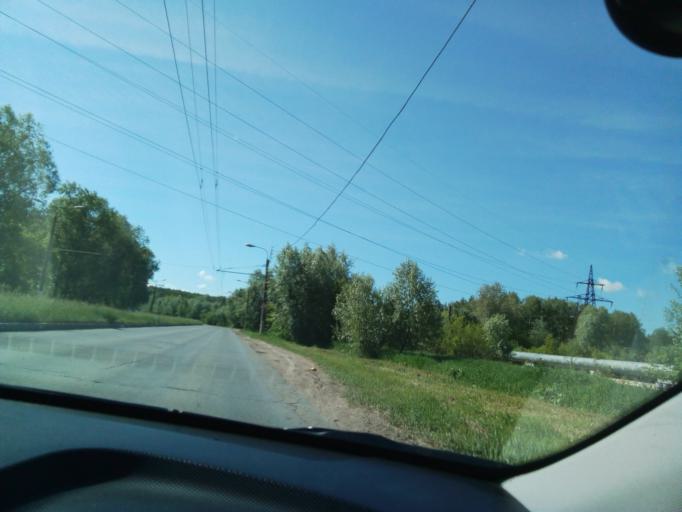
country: RU
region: Chuvashia
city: Novocheboksarsk
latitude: 56.0874
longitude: 47.5018
